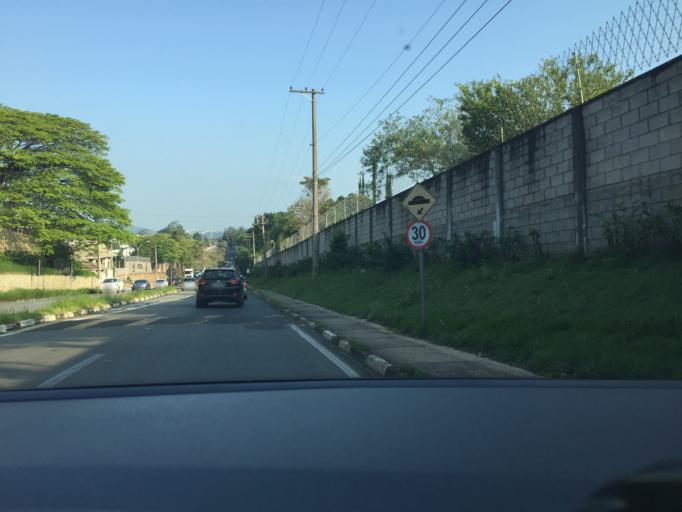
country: BR
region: Sao Paulo
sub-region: Vinhedo
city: Vinhedo
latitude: -23.0242
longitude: -46.9974
